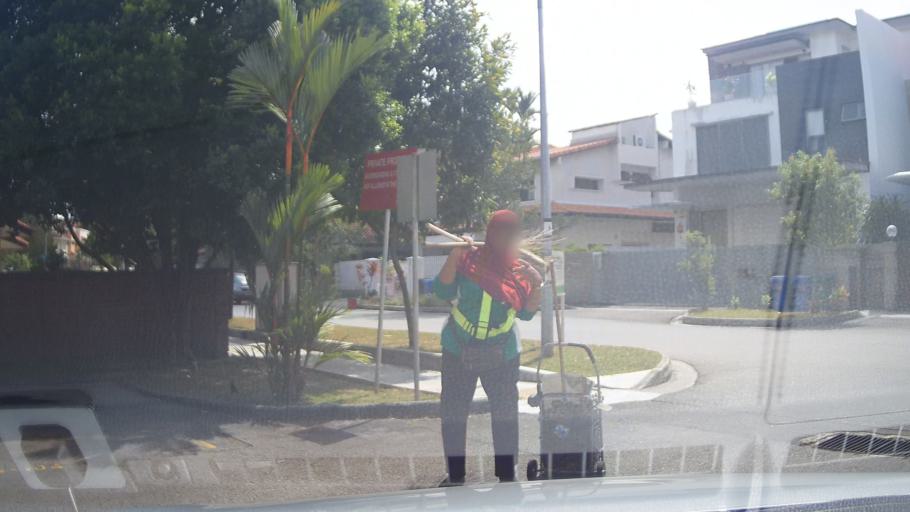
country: SG
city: Singapore
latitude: 1.3202
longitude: 103.7541
